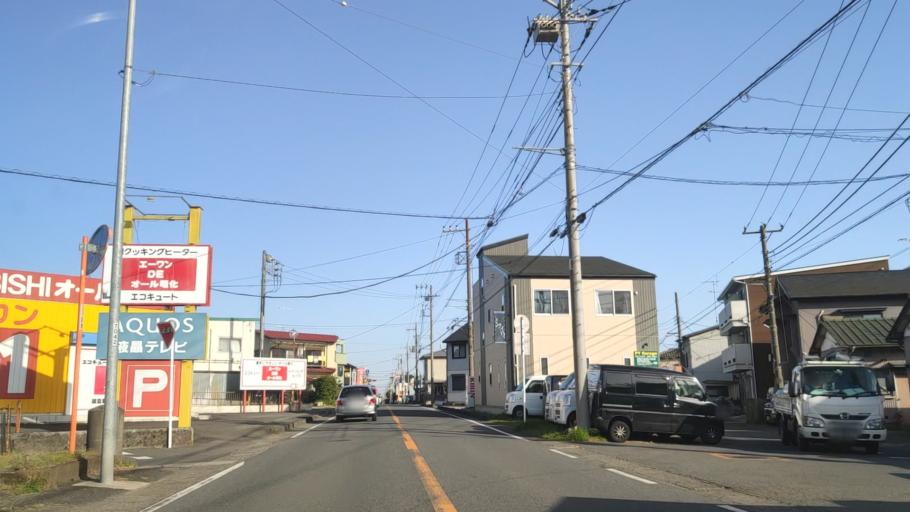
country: JP
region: Kanagawa
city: Zama
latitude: 35.5048
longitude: 139.3494
